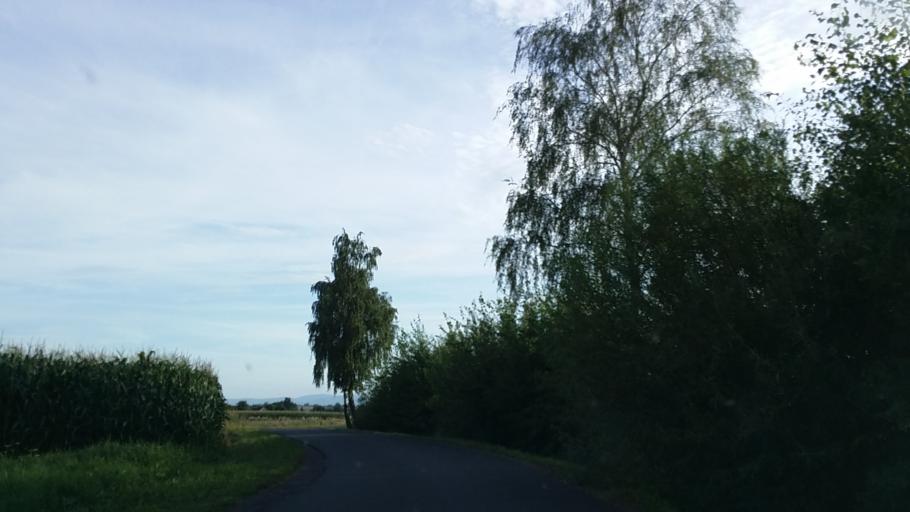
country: PL
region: Lesser Poland Voivodeship
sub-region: Powiat oswiecimski
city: Przeciszow
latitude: 49.9909
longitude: 19.4011
